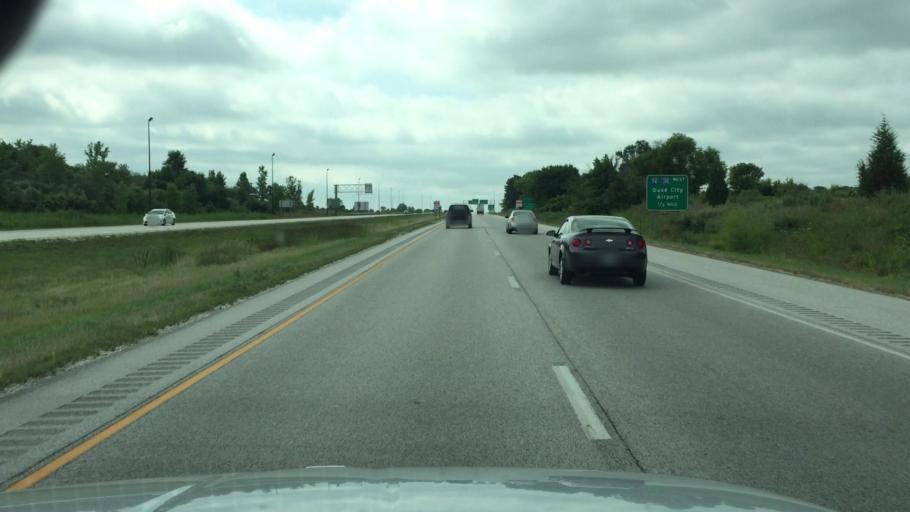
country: US
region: Illinois
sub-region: Henry County
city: Green Rock
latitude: 41.4499
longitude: -90.3344
